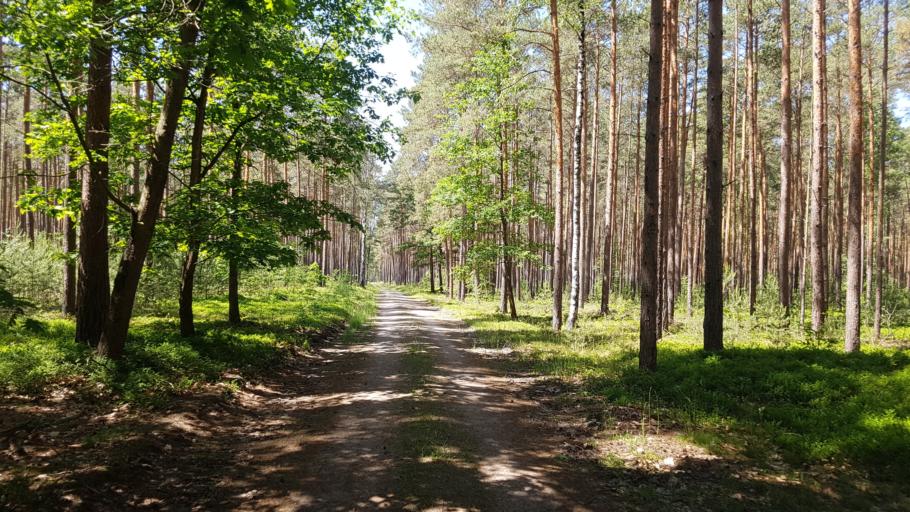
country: DE
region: Brandenburg
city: Ruckersdorf
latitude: 51.5454
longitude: 13.5709
